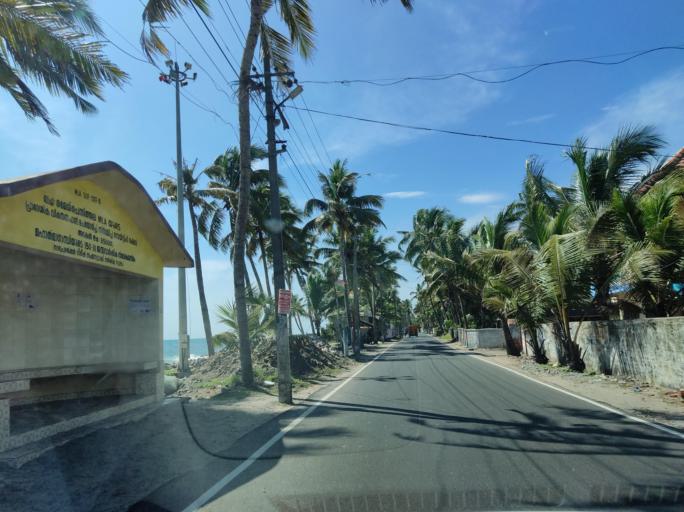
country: IN
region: Kerala
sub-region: Alappuzha
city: Kayankulam
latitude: 9.2544
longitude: 76.4090
